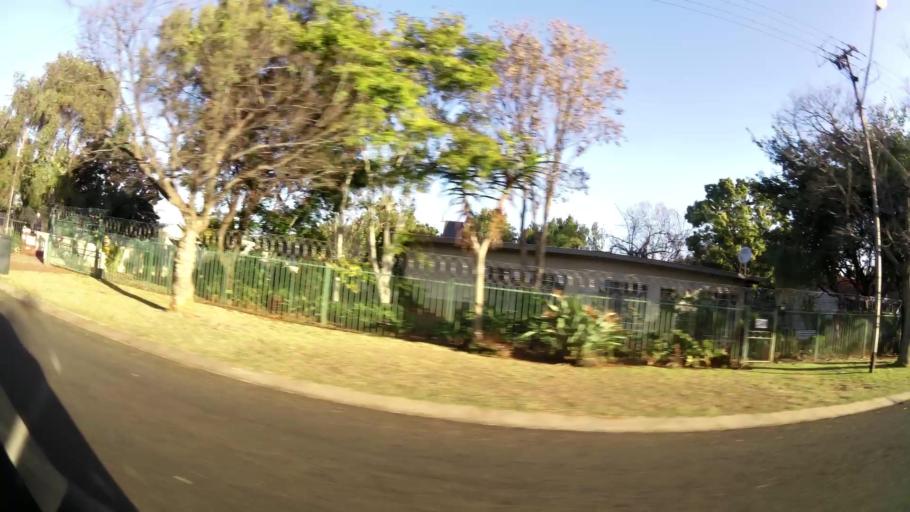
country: ZA
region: Gauteng
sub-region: City of Tshwane Metropolitan Municipality
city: Pretoria
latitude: -25.7043
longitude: 28.2584
